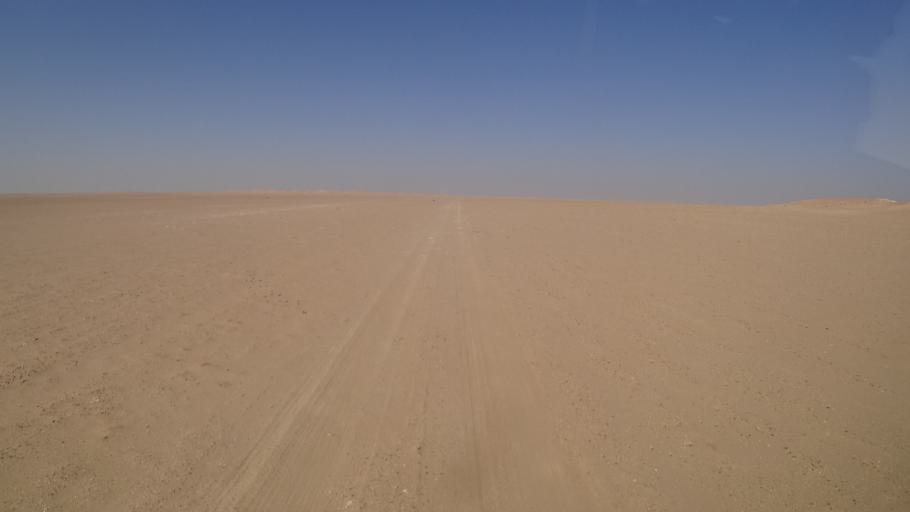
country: YE
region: Al Mahrah
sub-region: Shahan
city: Shihan as Sufla
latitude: 18.5657
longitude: 52.8350
